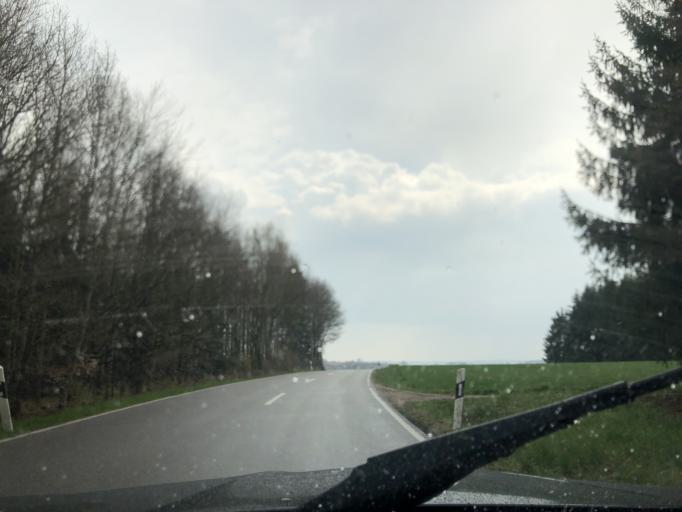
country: DE
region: Bavaria
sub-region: Upper Bavaria
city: Wolfersdorf
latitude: 48.4944
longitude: 11.6917
